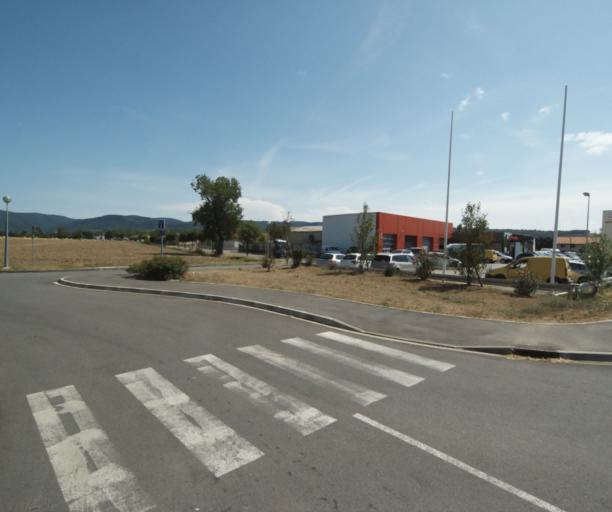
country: FR
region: Midi-Pyrenees
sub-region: Departement de la Haute-Garonne
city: Revel
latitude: 43.4669
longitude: 2.0099
